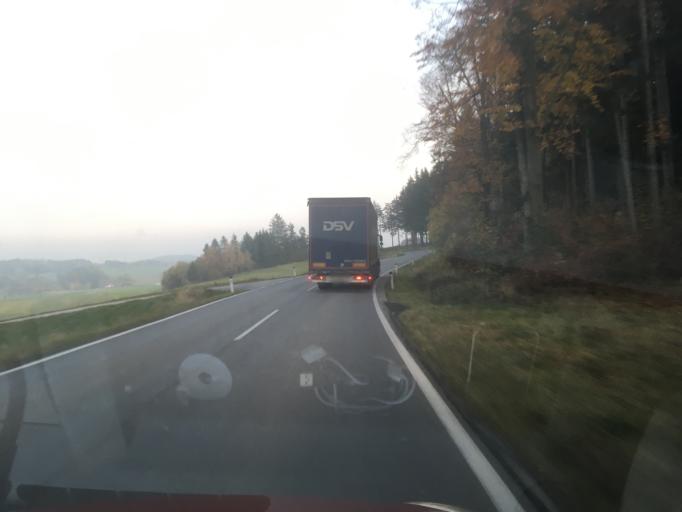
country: AT
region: Lower Austria
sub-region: Politischer Bezirk Zwettl
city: Gross-Gerungs
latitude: 48.5615
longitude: 14.9991
